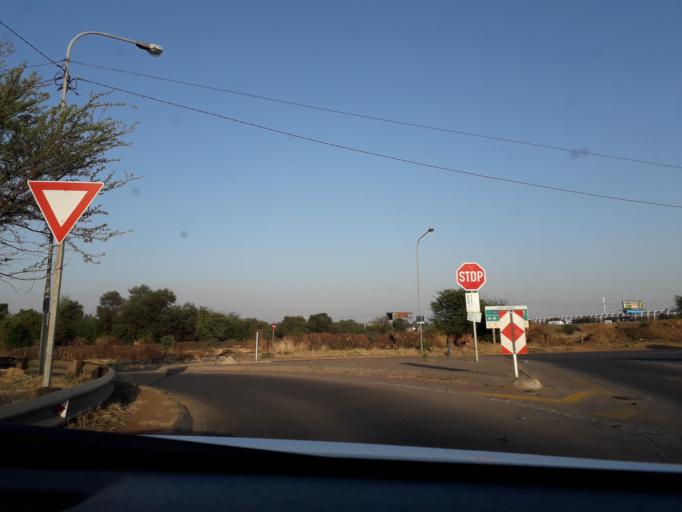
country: ZA
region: Gauteng
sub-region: City of Tshwane Metropolitan Municipality
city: Centurion
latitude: -25.8632
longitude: 28.1943
